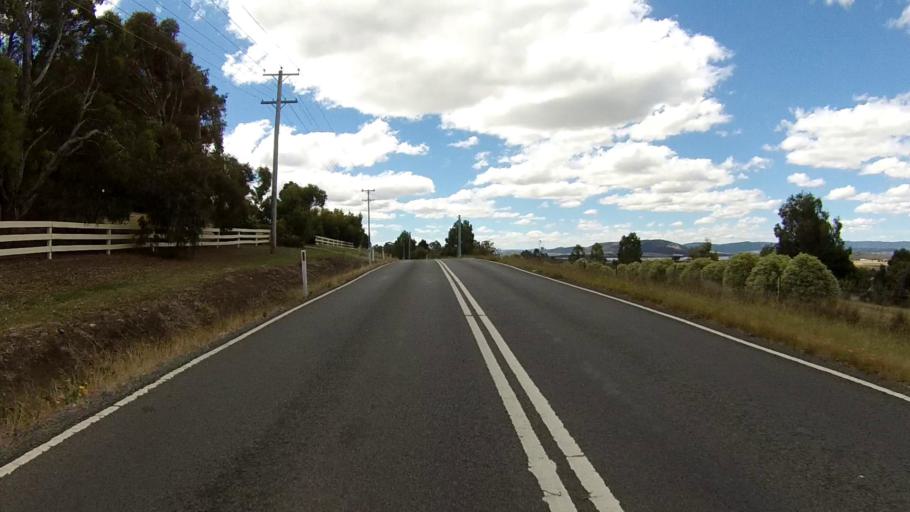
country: AU
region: Tasmania
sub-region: Clarence
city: Acton Park
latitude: -42.8580
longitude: 147.4747
